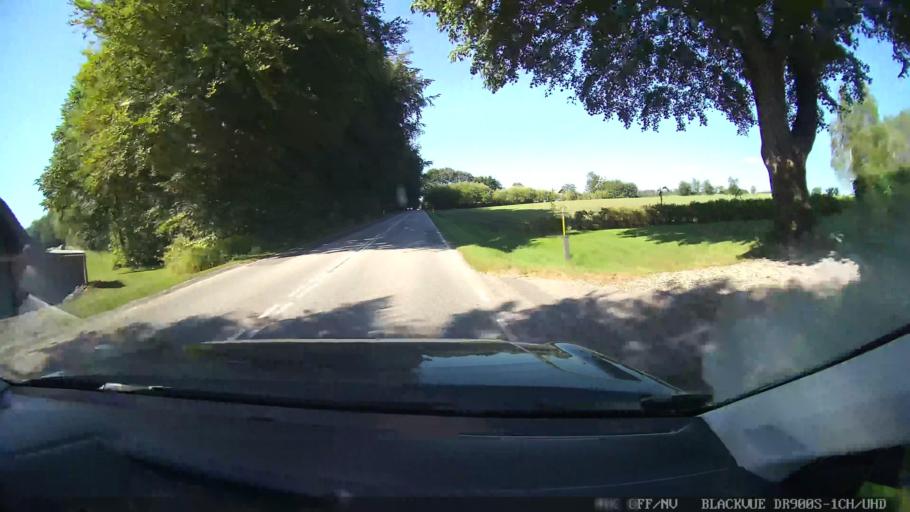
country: DK
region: North Denmark
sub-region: Mariagerfjord Kommune
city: Mariager
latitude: 56.6134
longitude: 9.9885
